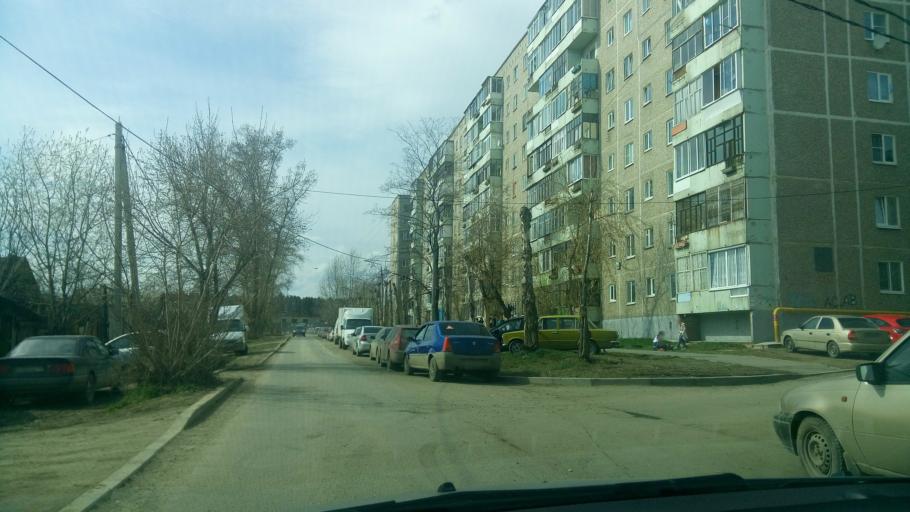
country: RU
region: Sverdlovsk
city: Verkhnyaya Pyshma
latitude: 56.9095
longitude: 60.5856
